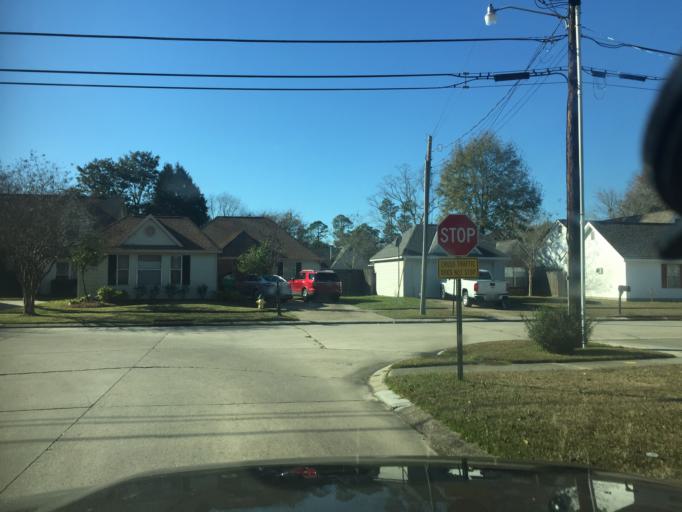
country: US
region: Louisiana
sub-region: Saint Tammany Parish
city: Slidell
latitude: 30.2934
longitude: -89.7548
